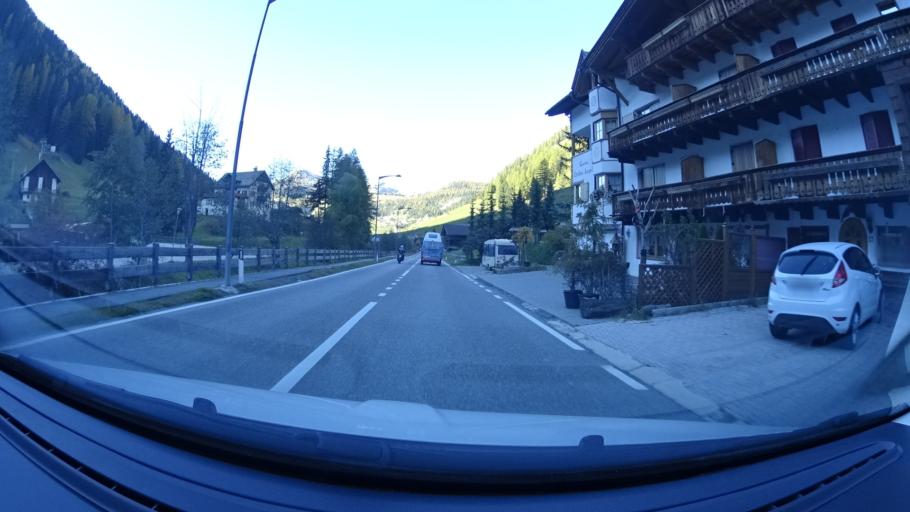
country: IT
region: Trentino-Alto Adige
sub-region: Bolzano
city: Selva
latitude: 46.5469
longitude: 11.7684
